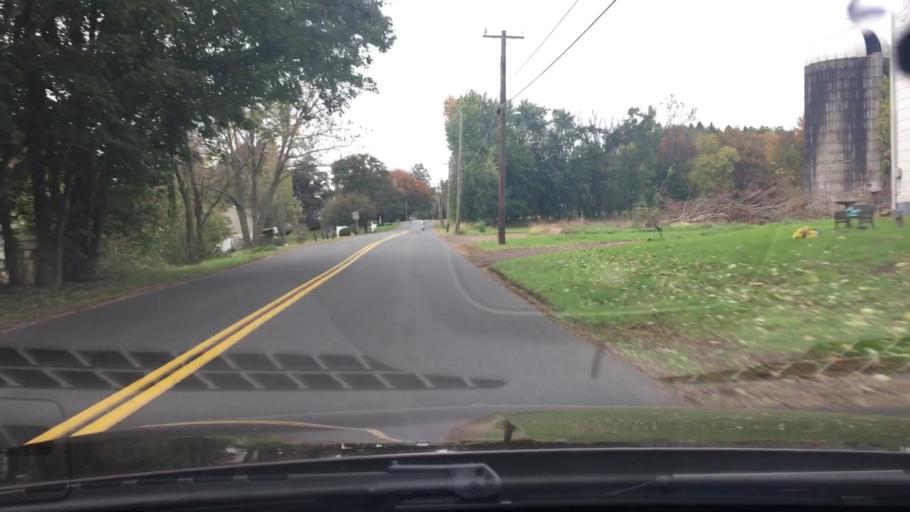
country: US
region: Connecticut
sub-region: Tolland County
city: Ellington
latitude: 41.9246
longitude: -72.4767
